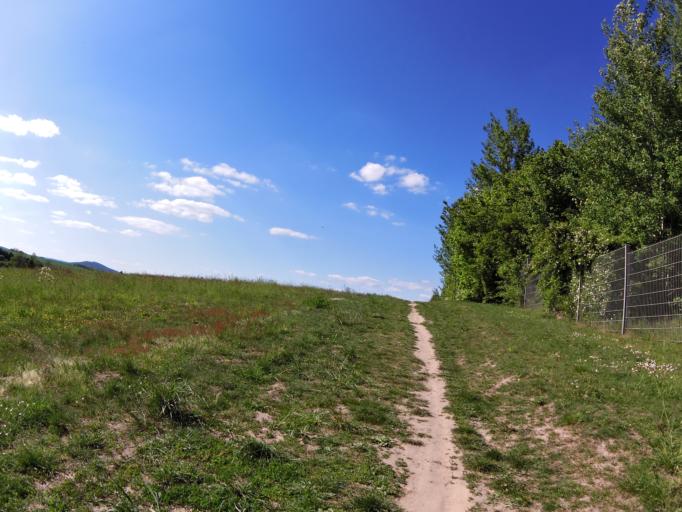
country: DE
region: Thuringia
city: Bad Salzungen
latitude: 50.8020
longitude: 10.2173
